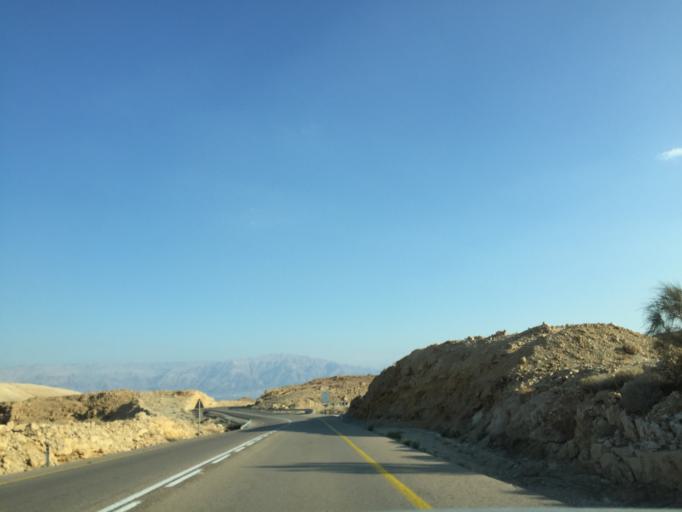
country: IL
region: Southern District
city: `En Boqeq
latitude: 31.1618
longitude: 35.3260
